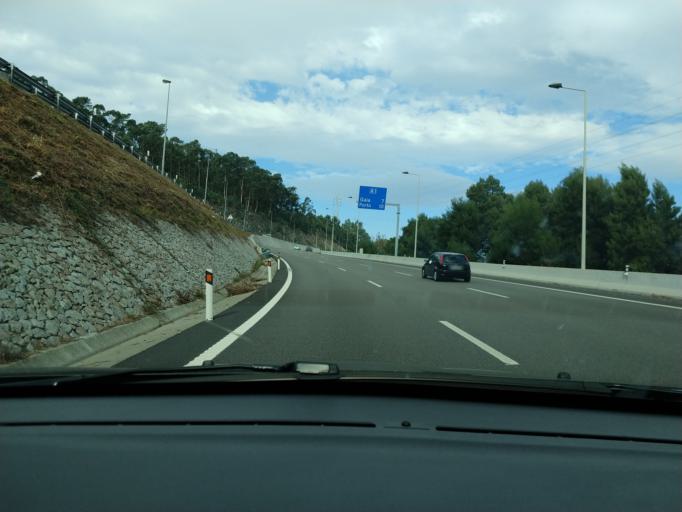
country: PT
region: Porto
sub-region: Vila Nova de Gaia
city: Perozinho
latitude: 41.0778
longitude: -8.5792
